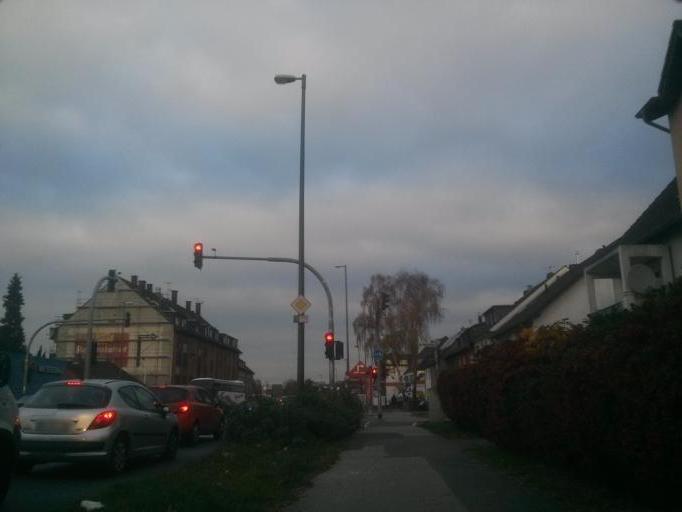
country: DE
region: North Rhine-Westphalia
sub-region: Regierungsbezirk Koln
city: Poll
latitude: 50.9117
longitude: 7.0010
